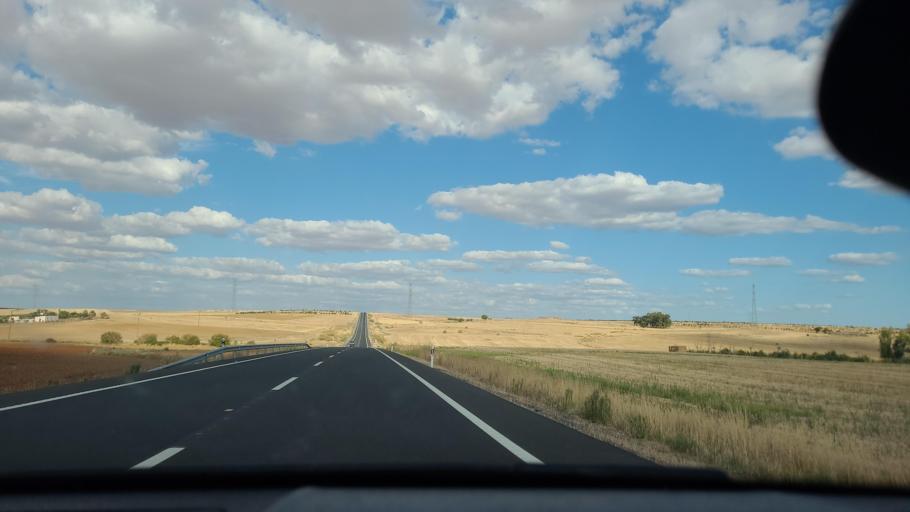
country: ES
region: Extremadura
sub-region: Provincia de Badajoz
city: Ahillones
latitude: 38.2535
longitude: -5.9169
